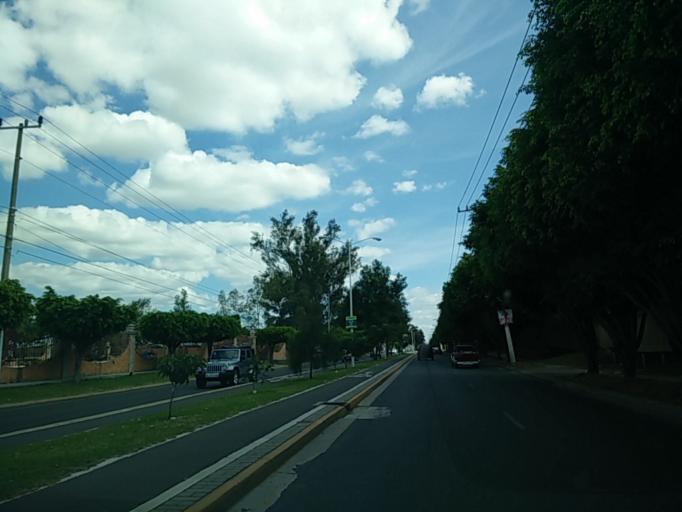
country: MX
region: Jalisco
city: Nuevo Mexico
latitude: 20.7305
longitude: -103.4470
